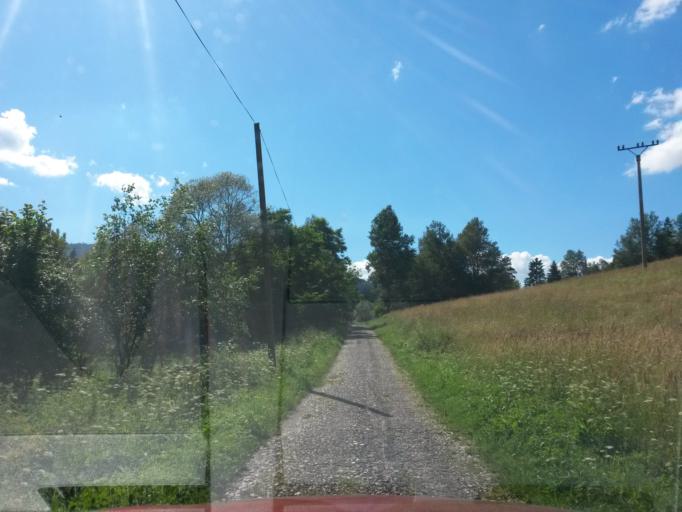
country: SK
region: Kosicky
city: Medzev
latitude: 48.7940
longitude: 20.7554
